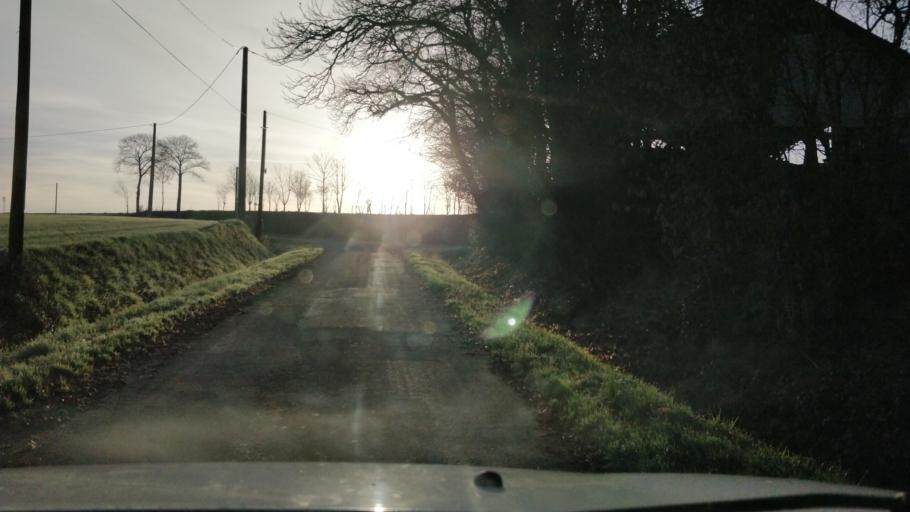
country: FR
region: Brittany
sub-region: Departement d'Ille-et-Vilaine
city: Bais
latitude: 48.0126
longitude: -1.3106
